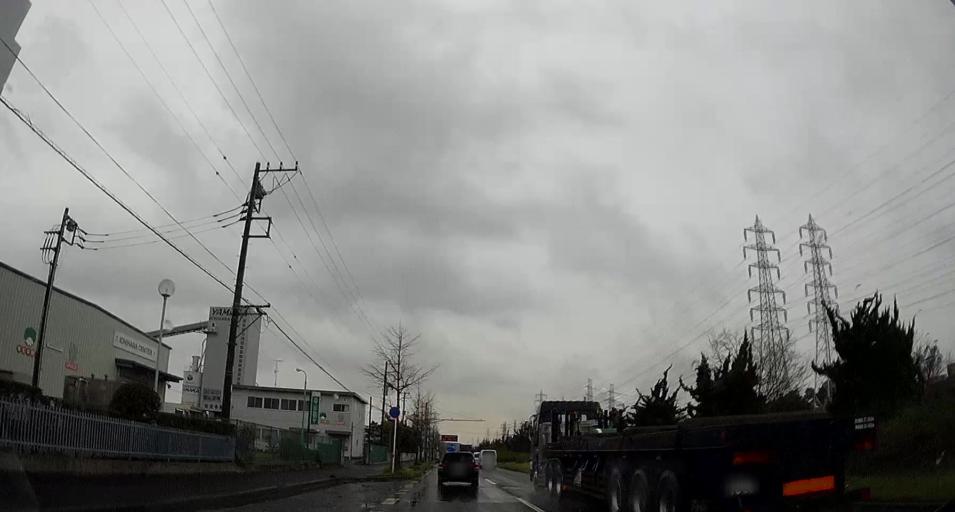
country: JP
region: Chiba
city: Ichihara
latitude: 35.4800
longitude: 140.0351
